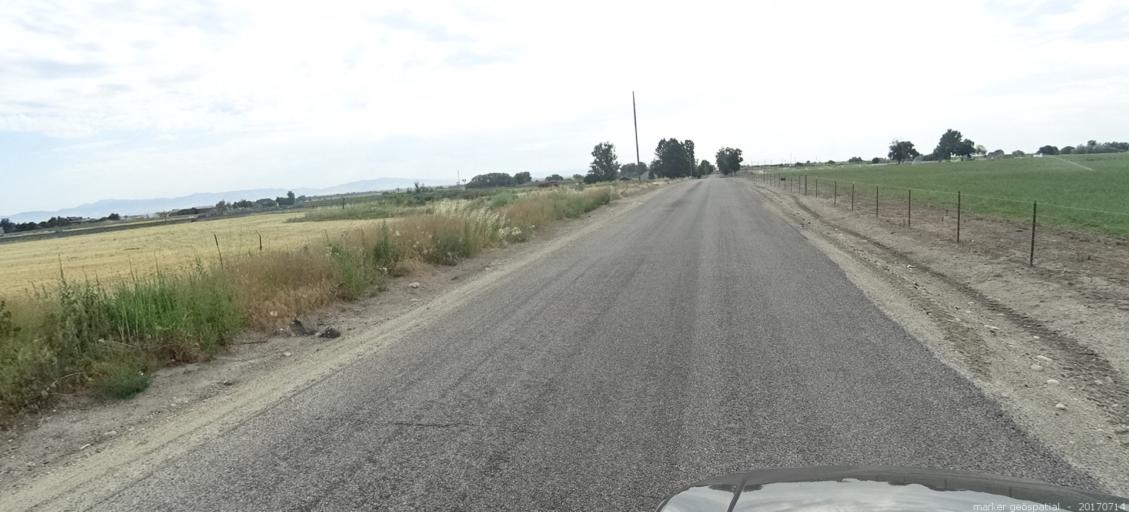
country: US
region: Idaho
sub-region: Ada County
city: Kuna
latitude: 43.4593
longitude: -116.3625
